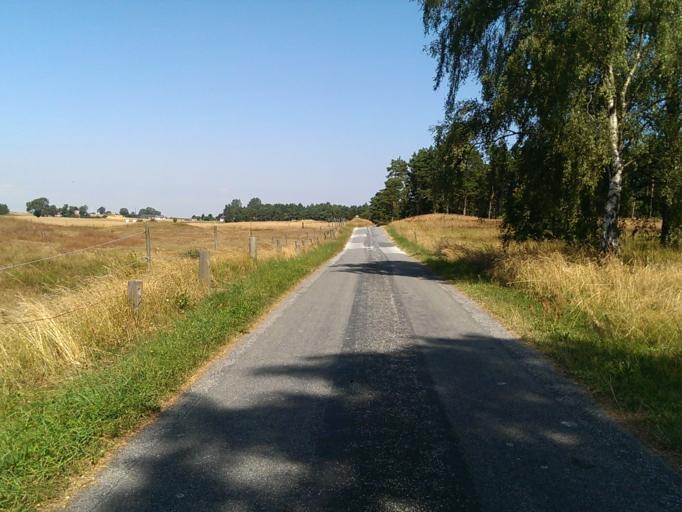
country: SE
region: Skane
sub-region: Simrishamns Kommun
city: Simrishamn
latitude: 55.4254
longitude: 14.2196
